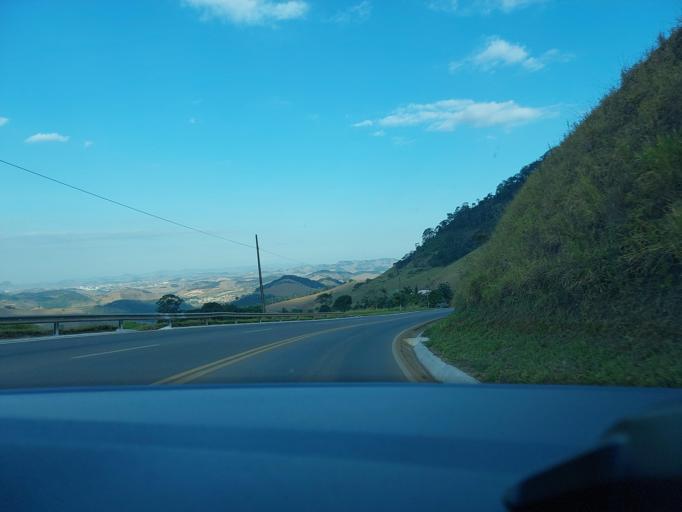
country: BR
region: Minas Gerais
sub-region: Muriae
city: Muriae
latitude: -21.0825
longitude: -42.4909
